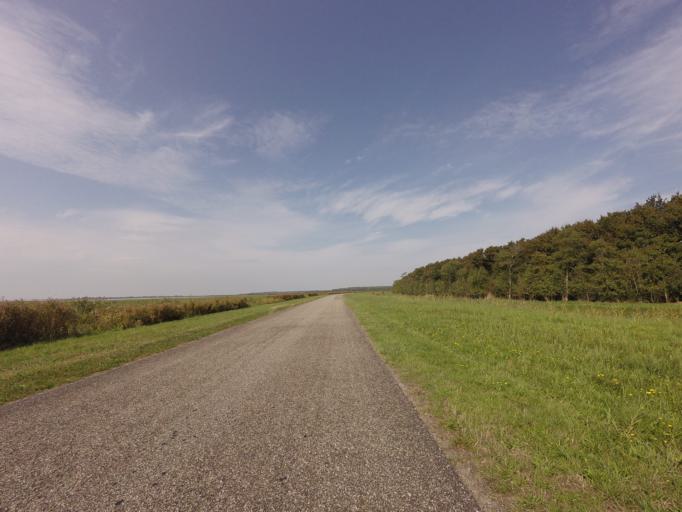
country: NL
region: Groningen
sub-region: Gemeente De Marne
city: Ulrum
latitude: 53.3565
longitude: 6.2633
